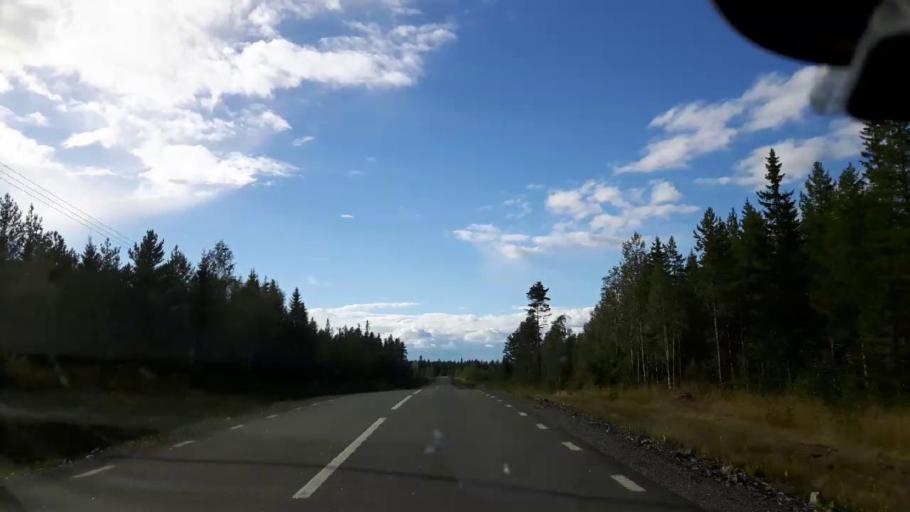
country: SE
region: Jaemtland
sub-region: Stroemsunds Kommun
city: Stroemsund
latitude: 63.5768
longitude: 15.7461
